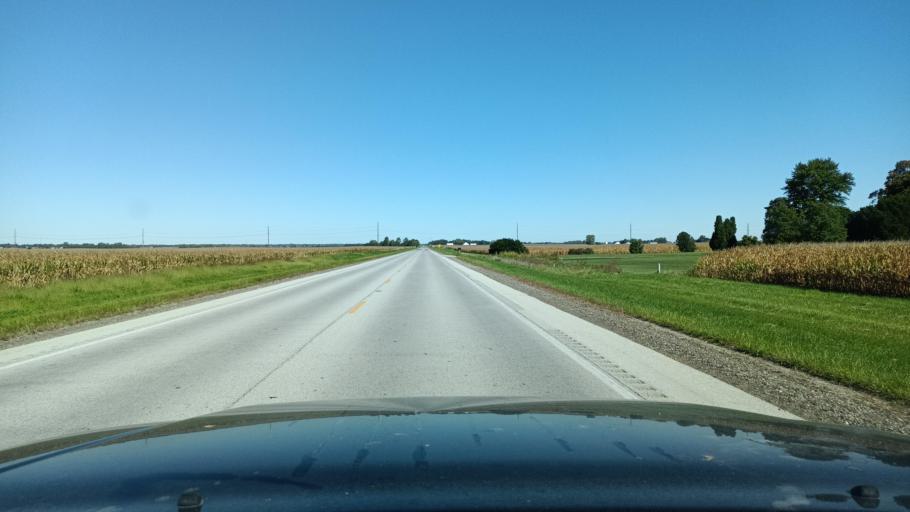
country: US
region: Illinois
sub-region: Champaign County
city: Philo
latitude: 40.0491
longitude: -88.1617
